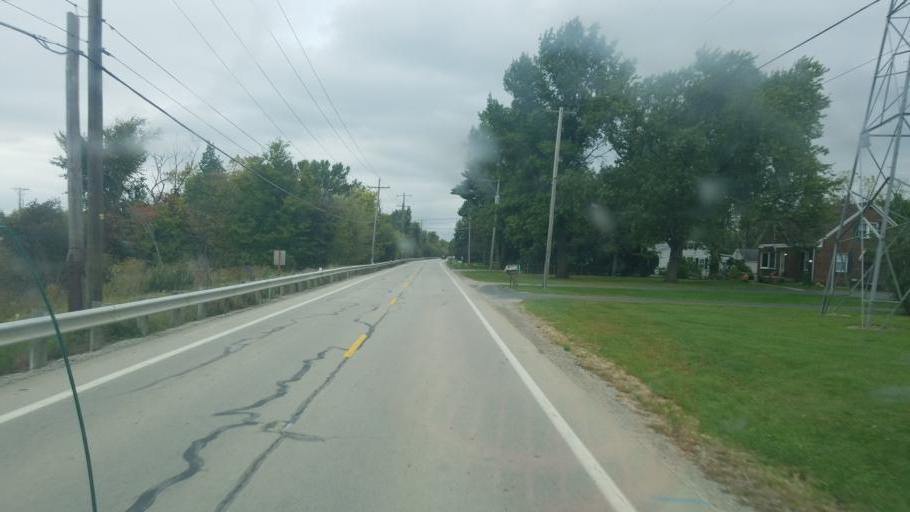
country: US
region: Ohio
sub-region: Wood County
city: Haskins
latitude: 41.4750
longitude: -83.7087
